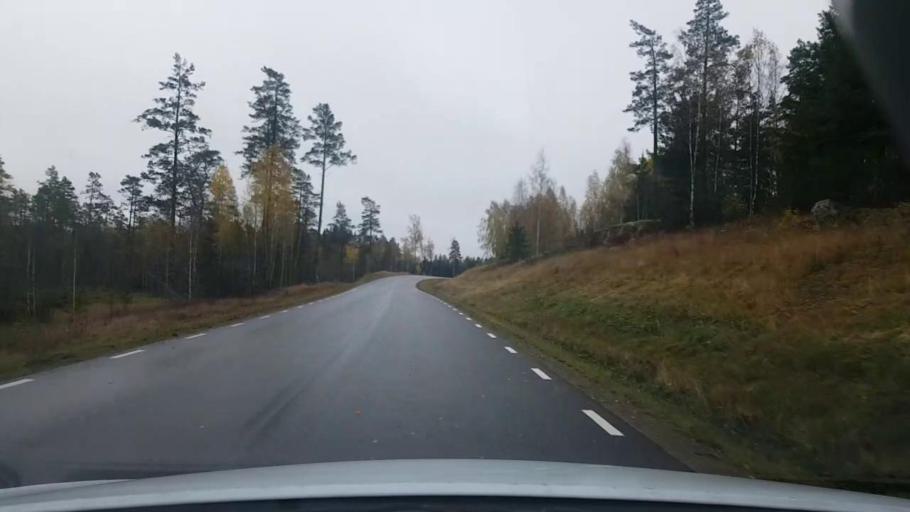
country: SE
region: Vaestra Goetaland
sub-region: Karlsborgs Kommun
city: Karlsborg
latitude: 58.6871
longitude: 14.5013
